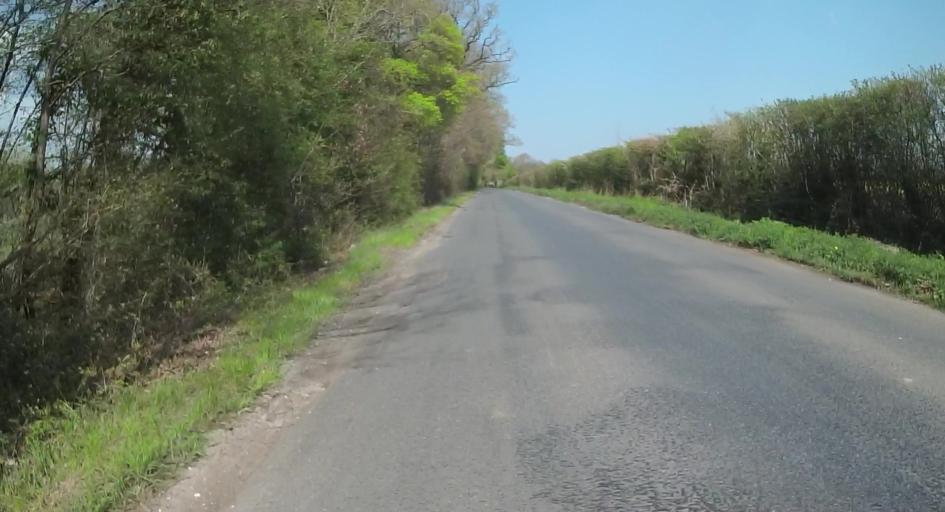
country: GB
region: England
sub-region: Hampshire
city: Basingstoke
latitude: 51.3173
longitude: -1.0809
